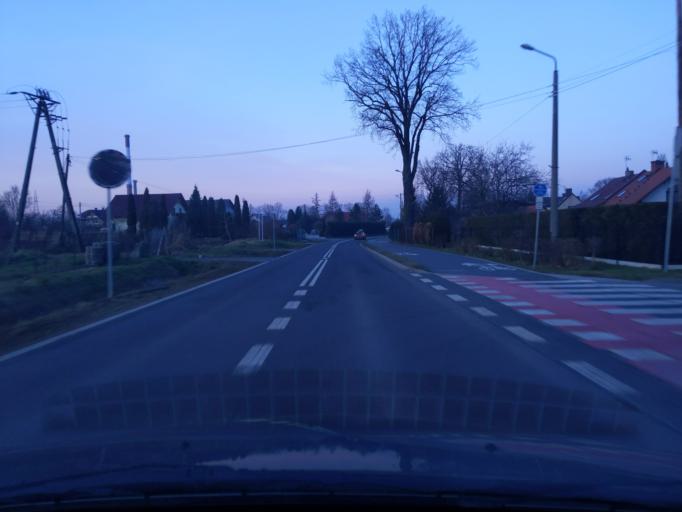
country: PL
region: Silesian Voivodeship
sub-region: Powiat pszczynski
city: Pszczyna
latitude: 49.9568
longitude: 18.9333
